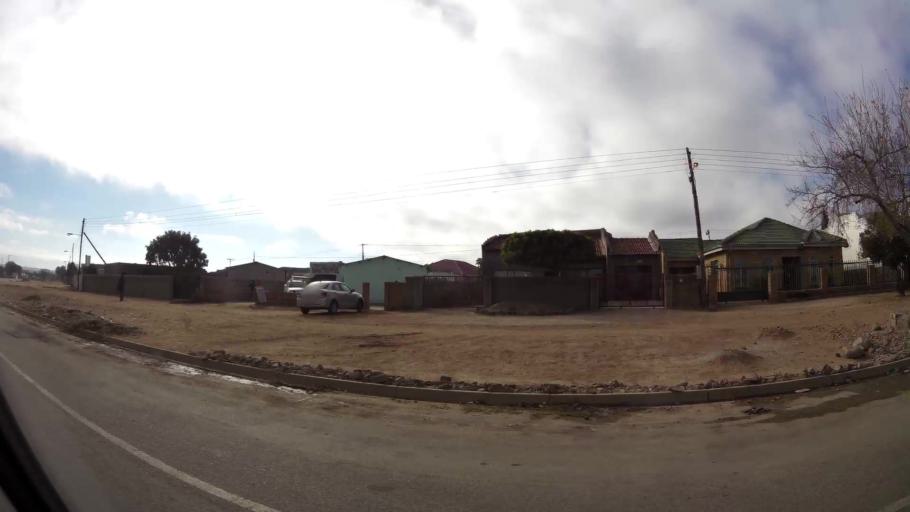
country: ZA
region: Limpopo
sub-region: Capricorn District Municipality
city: Polokwane
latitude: -23.8395
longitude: 29.3805
